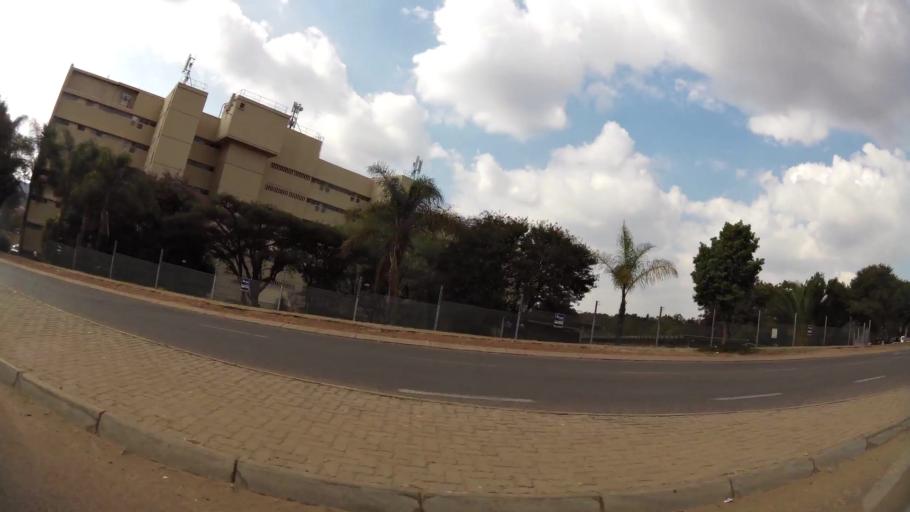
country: ZA
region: Gauteng
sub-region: City of Tshwane Metropolitan Municipality
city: Pretoria
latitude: -25.7831
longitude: 28.3004
